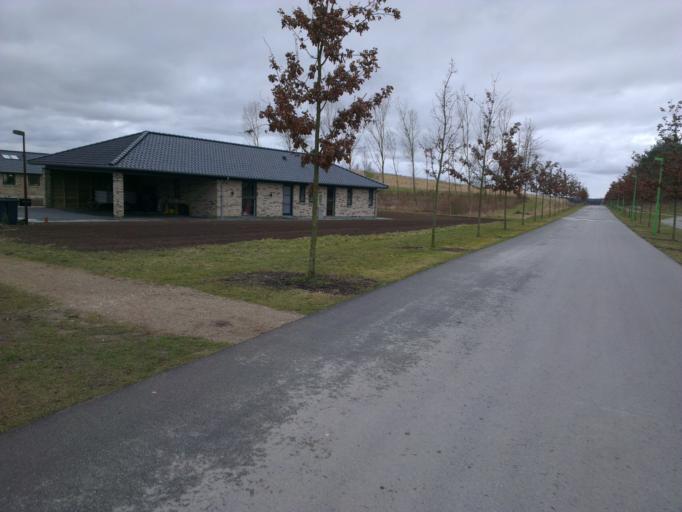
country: DK
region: Capital Region
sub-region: Frederikssund Kommune
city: Frederikssund
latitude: 55.8203
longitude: 12.0731
